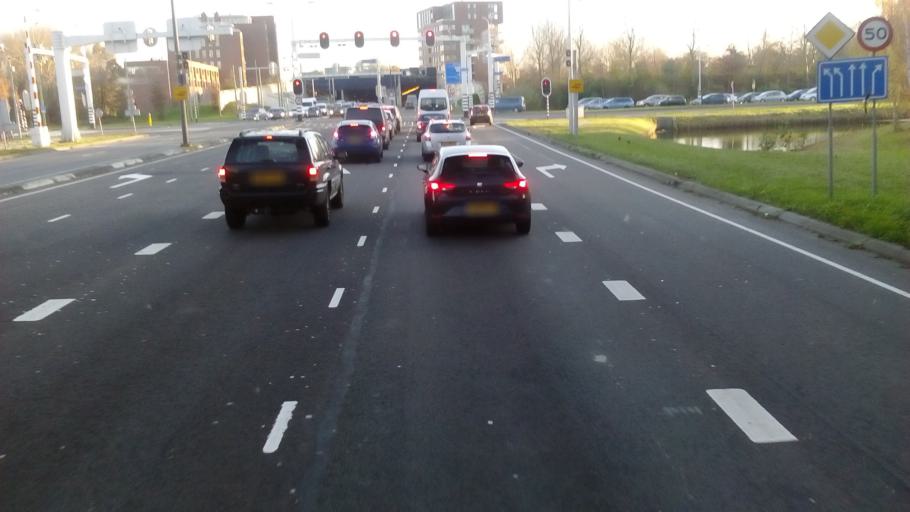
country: NL
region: South Holland
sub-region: Gemeente Leidschendam-Voorburg
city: Voorburg
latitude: 52.0875
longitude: 4.3776
